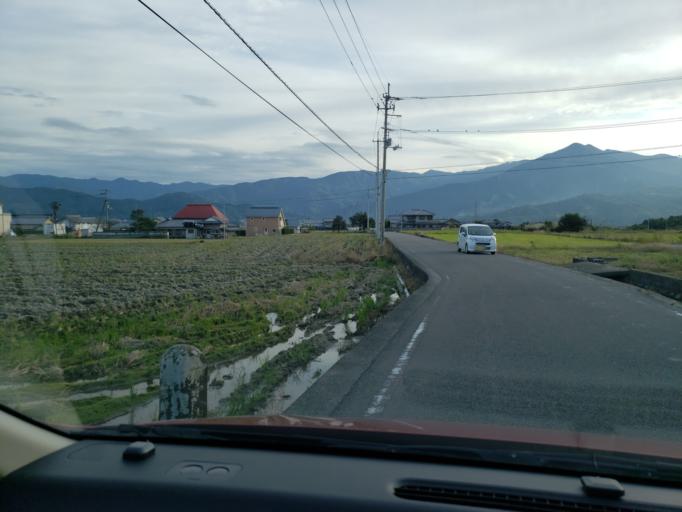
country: JP
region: Tokushima
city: Wakimachi
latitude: 34.0873
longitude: 134.2268
